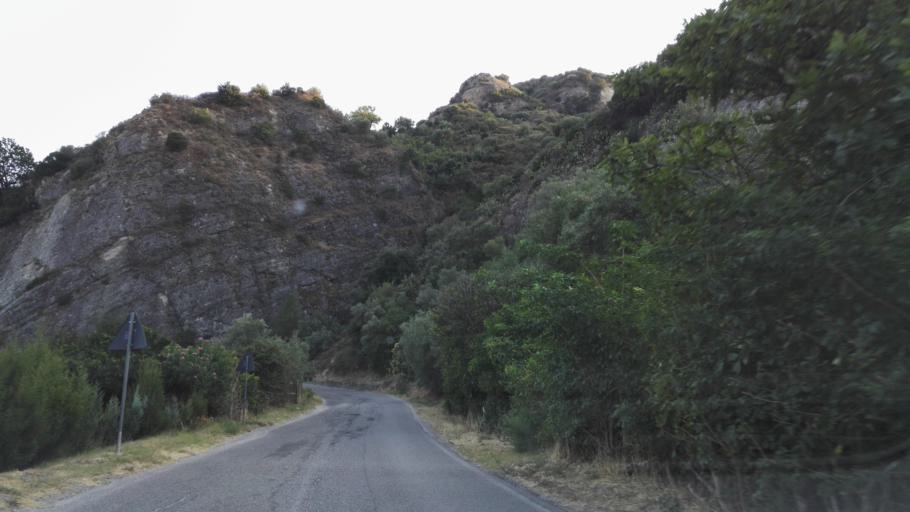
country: IT
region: Calabria
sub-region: Provincia di Reggio Calabria
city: Caulonia
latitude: 38.4024
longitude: 16.4108
